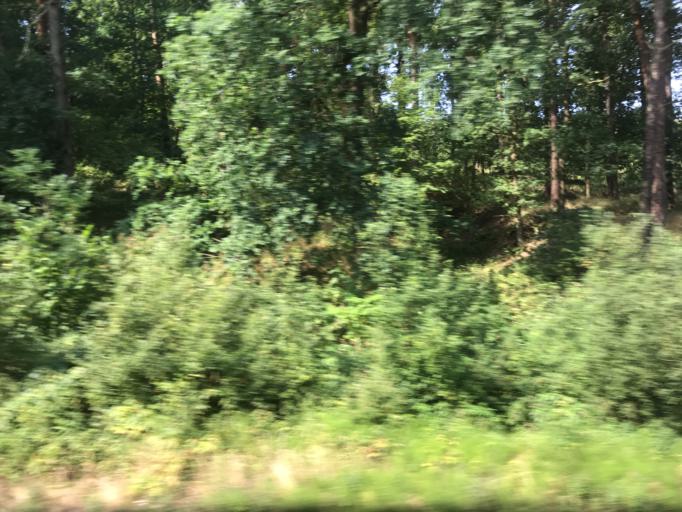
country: CZ
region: Central Bohemia
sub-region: Okres Benesov
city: Benesov
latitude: 49.8114
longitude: 14.7069
